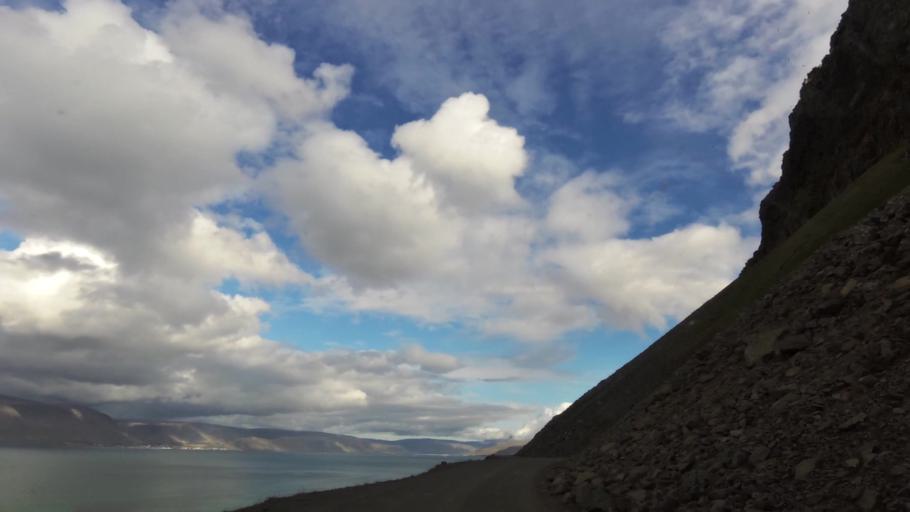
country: IS
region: West
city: Olafsvik
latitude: 65.6000
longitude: -24.1395
